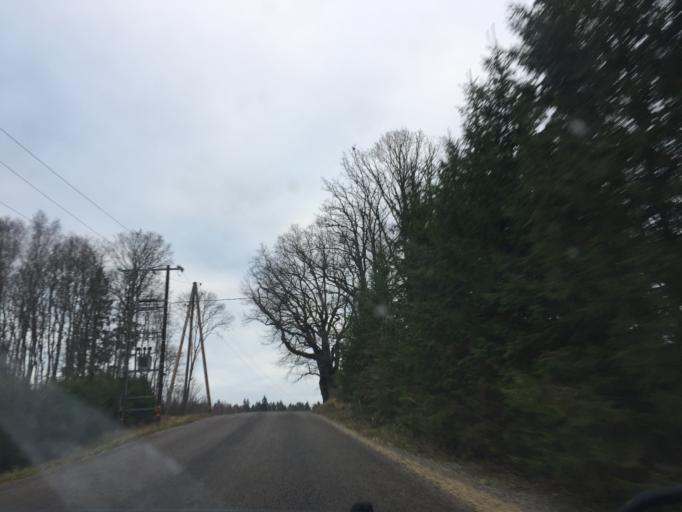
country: LV
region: Krimulda
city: Ragana
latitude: 57.1600
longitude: 24.7394
